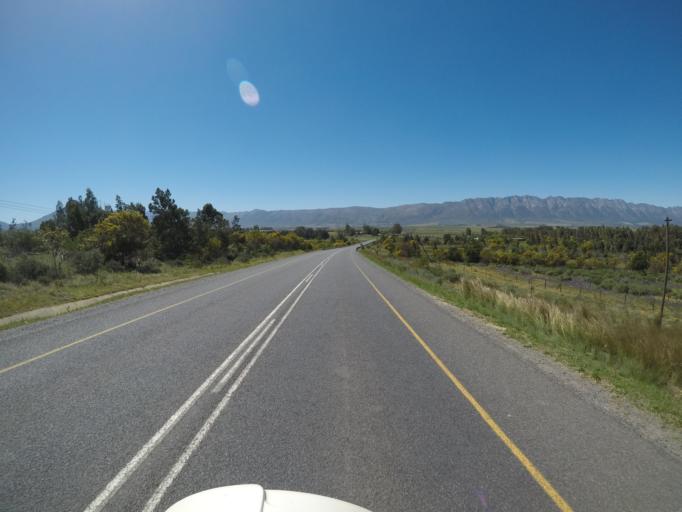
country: ZA
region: Western Cape
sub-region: Cape Winelands District Municipality
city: Ceres
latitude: -33.3120
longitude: 19.0971
